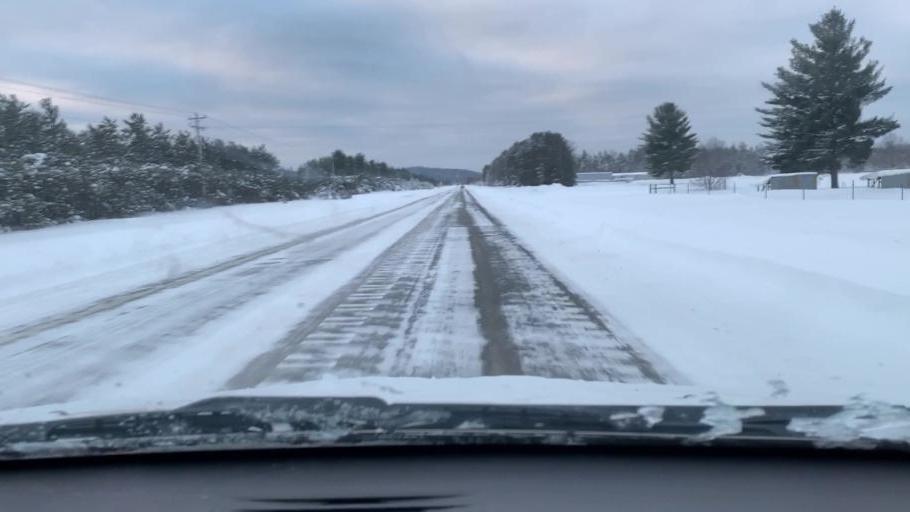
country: US
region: Michigan
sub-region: Antrim County
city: Mancelona
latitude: 44.9276
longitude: -85.0509
